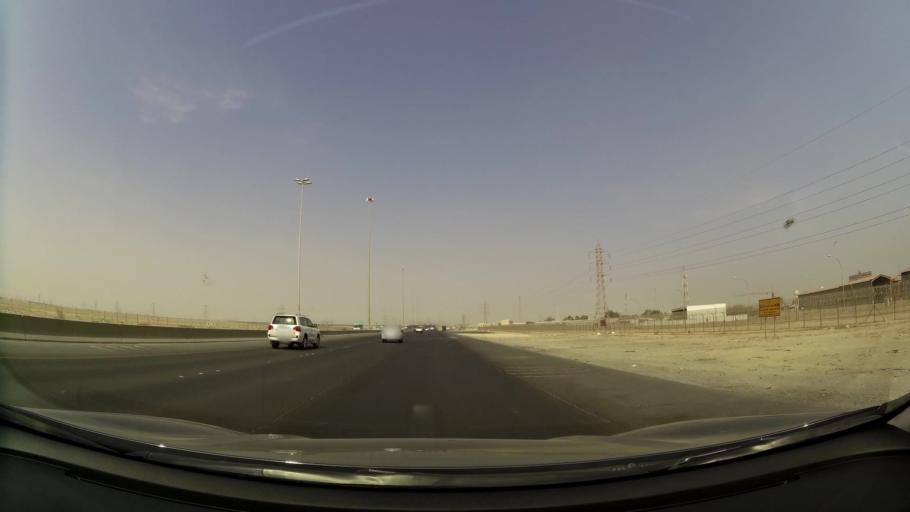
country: KW
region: Al Ahmadi
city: Al Fahahil
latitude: 29.0297
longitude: 48.1224
